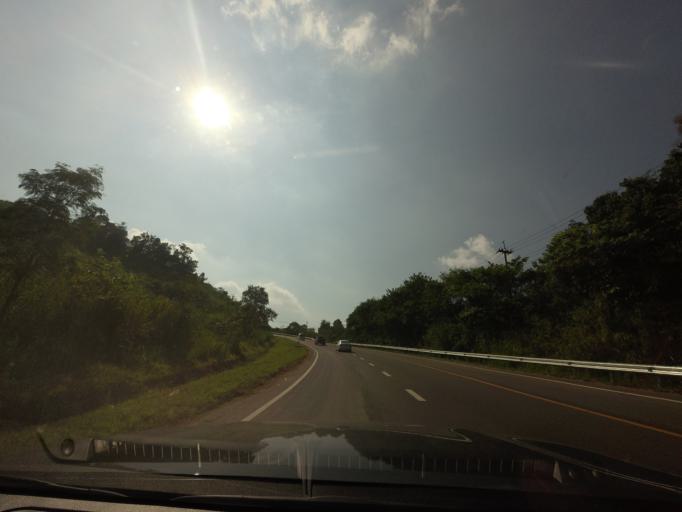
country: TH
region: Nan
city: Santi Suk
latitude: 18.9279
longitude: 100.8986
